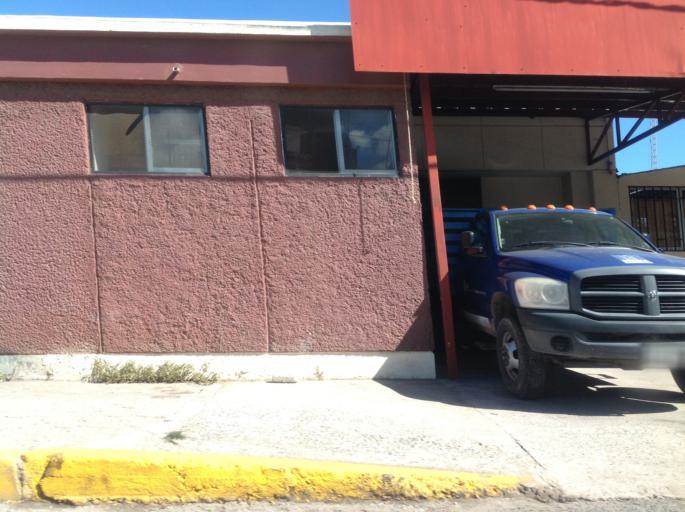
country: MX
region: Oaxaca
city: Ciudad de Huajuapam de Leon
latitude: 17.8114
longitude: -97.7728
